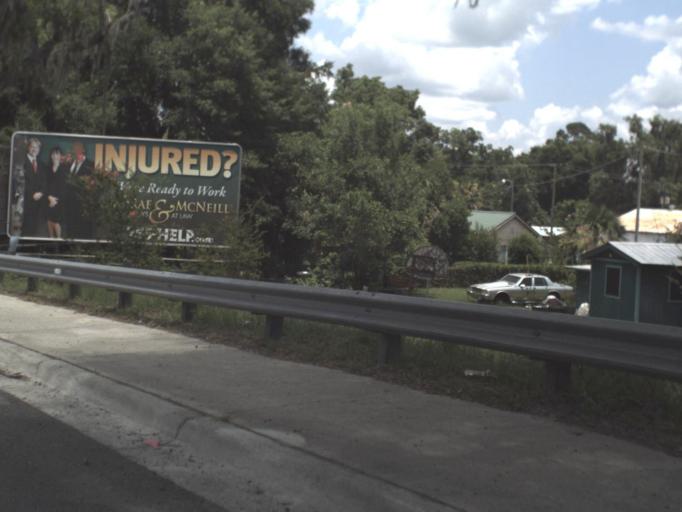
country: US
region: Florida
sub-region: Columbia County
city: Lake City
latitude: 30.1987
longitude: -82.6395
